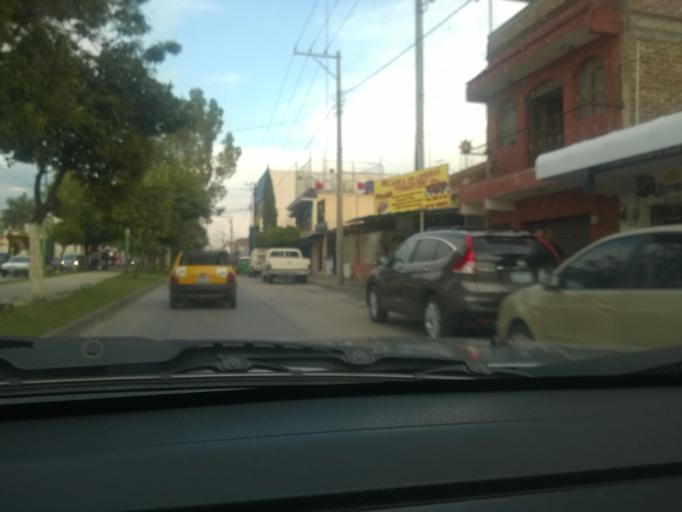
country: MX
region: Guanajuato
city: Leon
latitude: 21.1185
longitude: -101.6435
